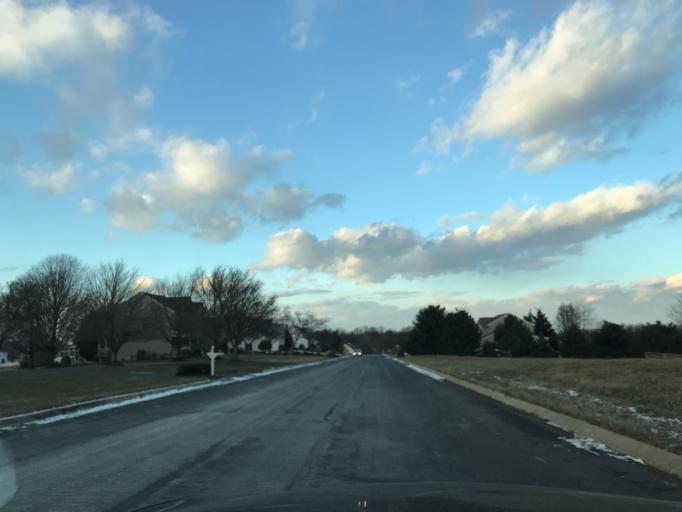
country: US
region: Maryland
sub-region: Harford County
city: Bel Air North
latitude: 39.5860
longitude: -76.3707
